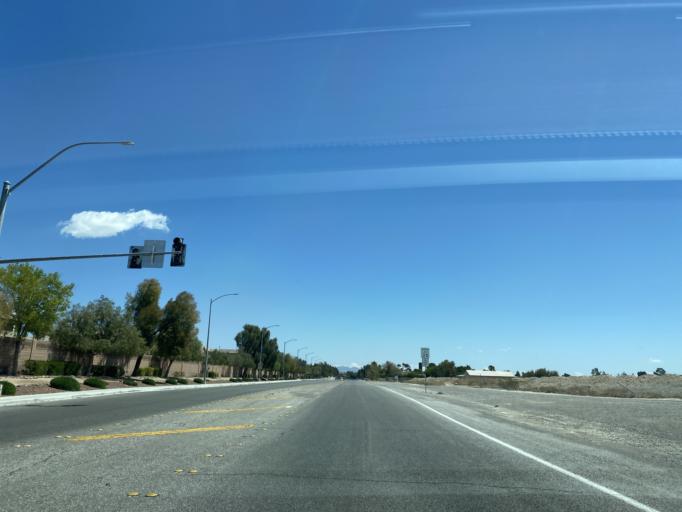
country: US
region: Nevada
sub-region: Clark County
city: North Las Vegas
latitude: 36.3051
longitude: -115.2331
